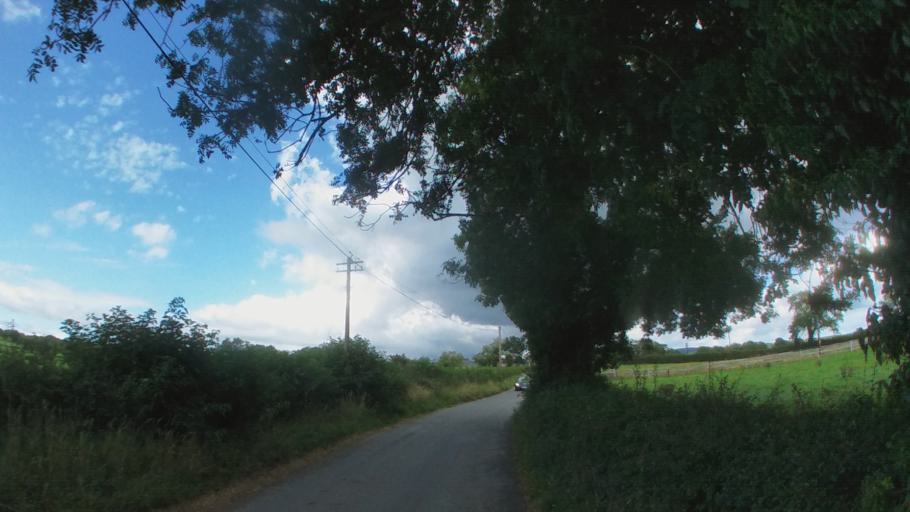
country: IE
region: Leinster
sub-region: Kilkenny
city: Kilkenny
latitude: 52.6733
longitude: -7.2272
